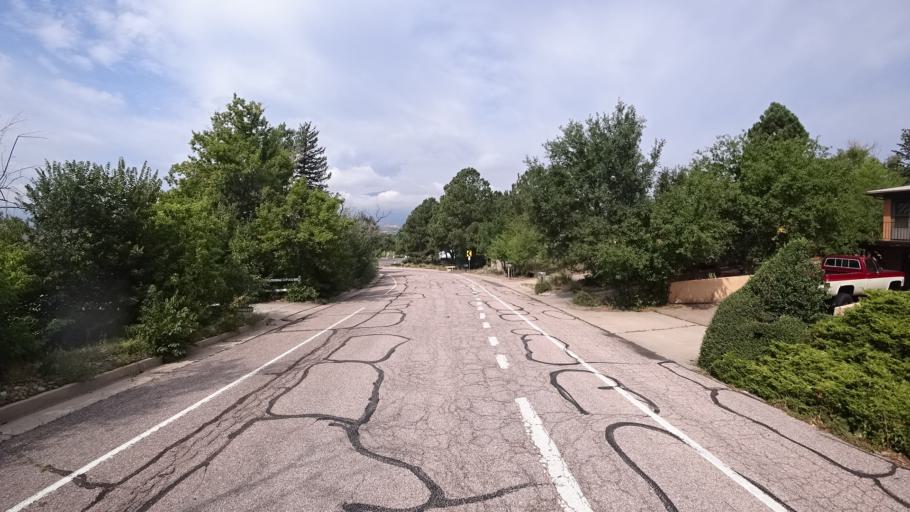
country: US
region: Colorado
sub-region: El Paso County
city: Colorado Springs
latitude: 38.8899
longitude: -104.8021
